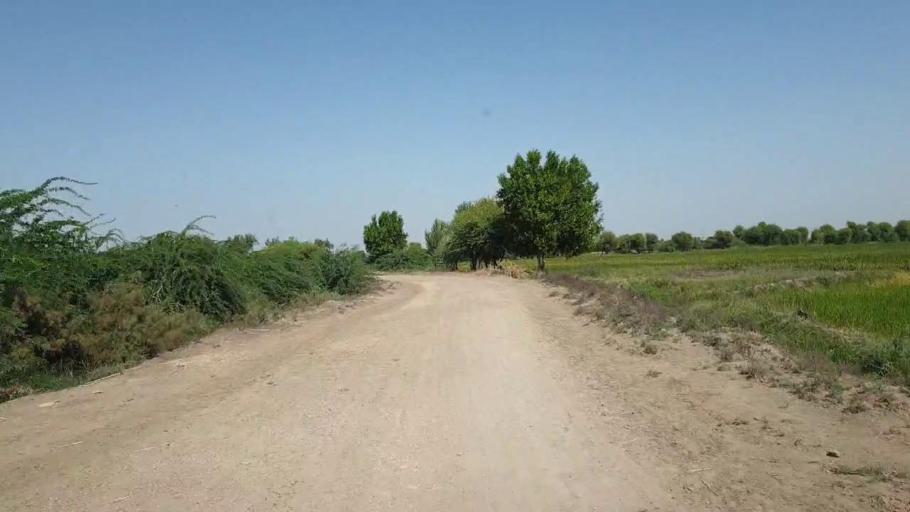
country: PK
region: Sindh
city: Tando Bago
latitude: 24.7391
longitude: 69.0435
